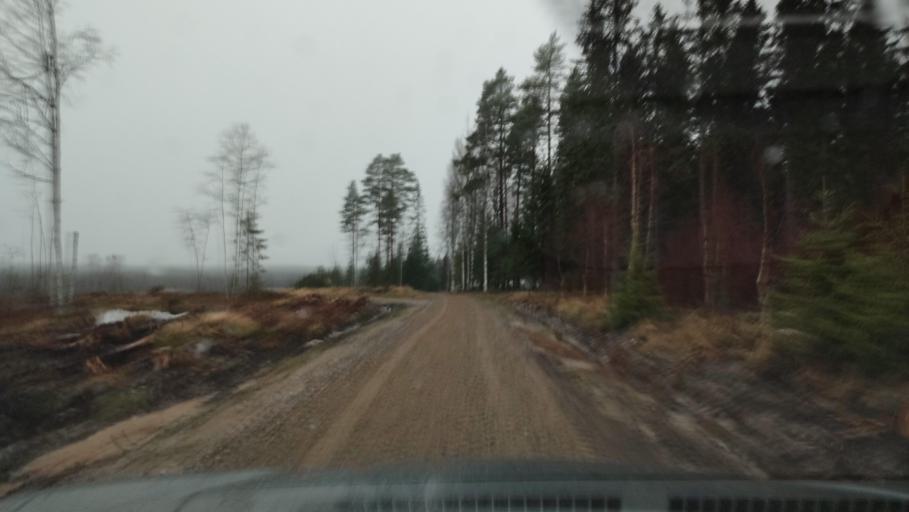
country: FI
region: Southern Ostrobothnia
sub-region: Suupohja
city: Karijoki
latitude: 62.1992
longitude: 21.7730
